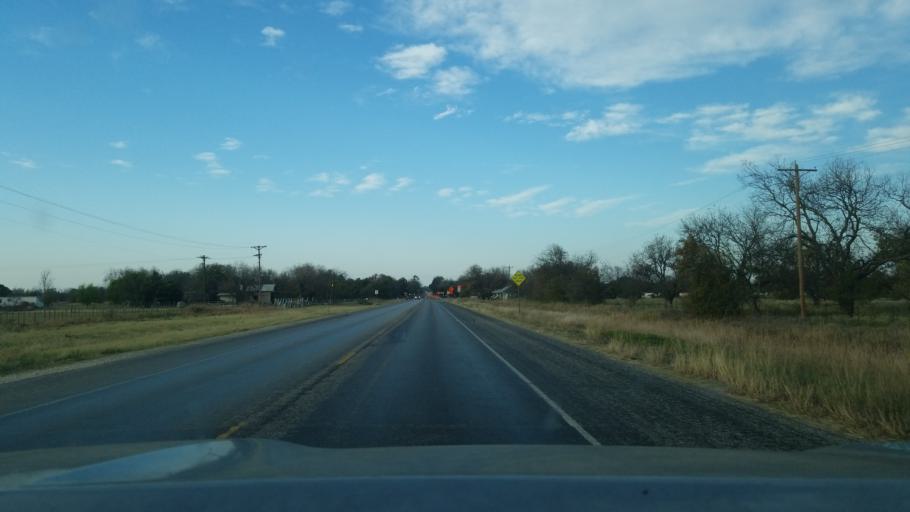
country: US
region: Texas
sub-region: Brown County
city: Lake Brownwood
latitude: 32.0829
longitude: -98.9640
